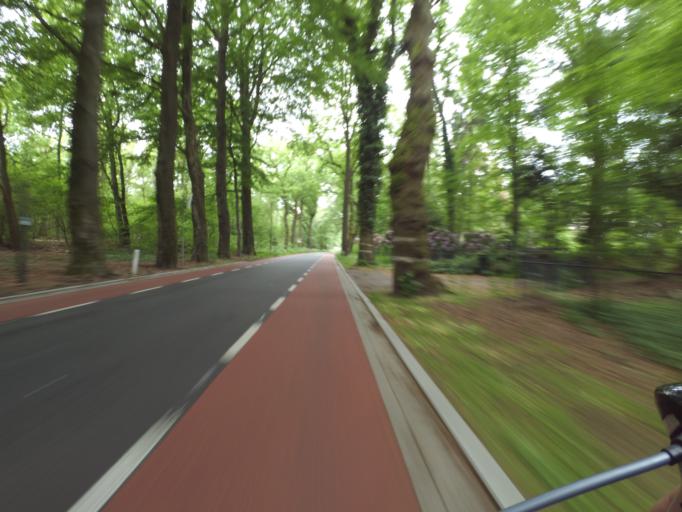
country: NL
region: Gelderland
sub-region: Gemeente Renkum
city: Doorwerth
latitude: 51.9933
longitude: 5.8043
